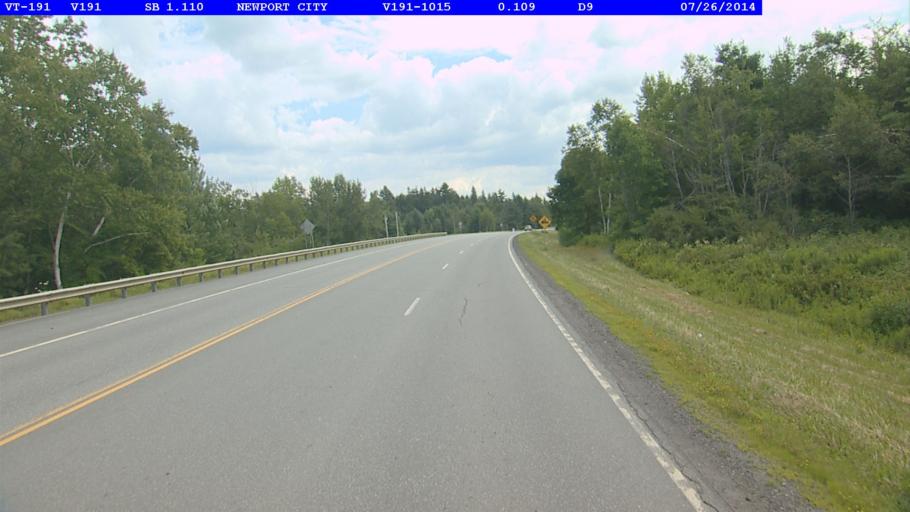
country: US
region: Vermont
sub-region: Orleans County
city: Newport
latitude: 44.9333
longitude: -72.1838
